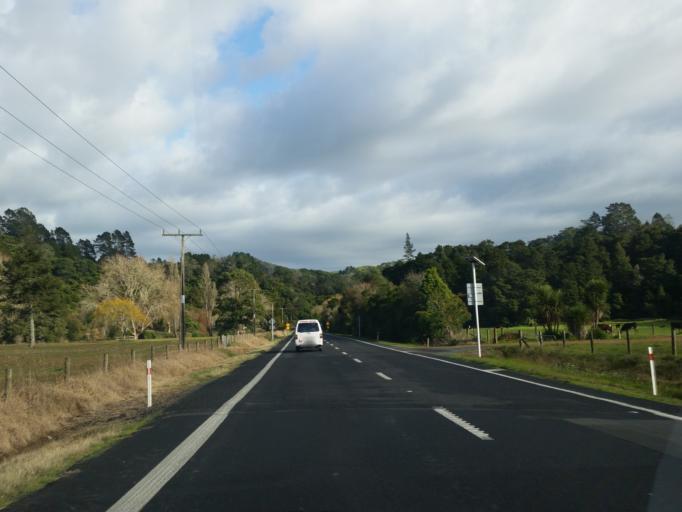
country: NZ
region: Waikato
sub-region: Hauraki District
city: Waihi
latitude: -37.4194
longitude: 175.7516
